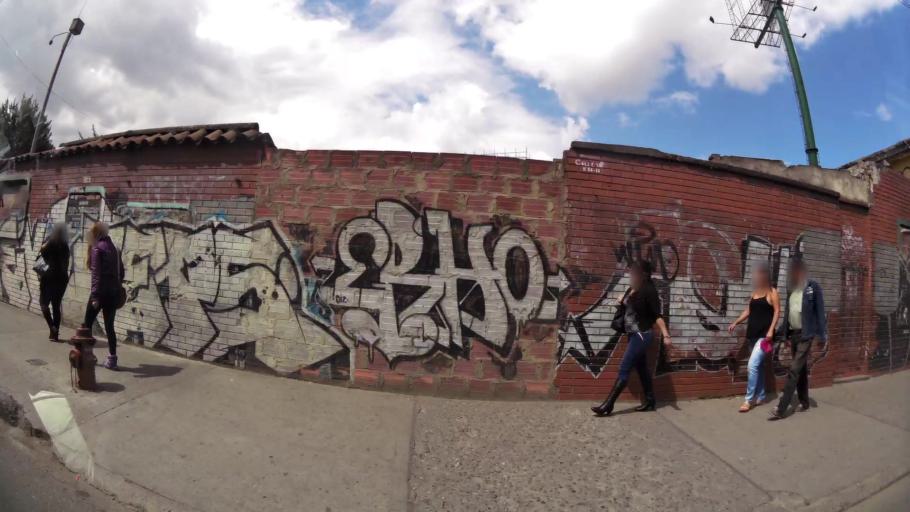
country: CO
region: Bogota D.C.
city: Bogota
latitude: 4.6374
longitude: -74.1178
